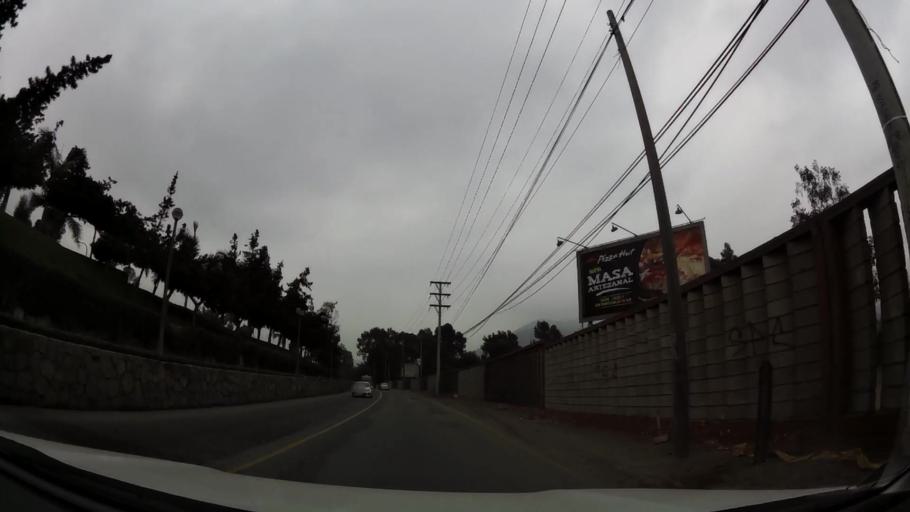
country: PE
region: Lima
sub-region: Lima
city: La Molina
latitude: -12.0774
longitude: -76.9330
